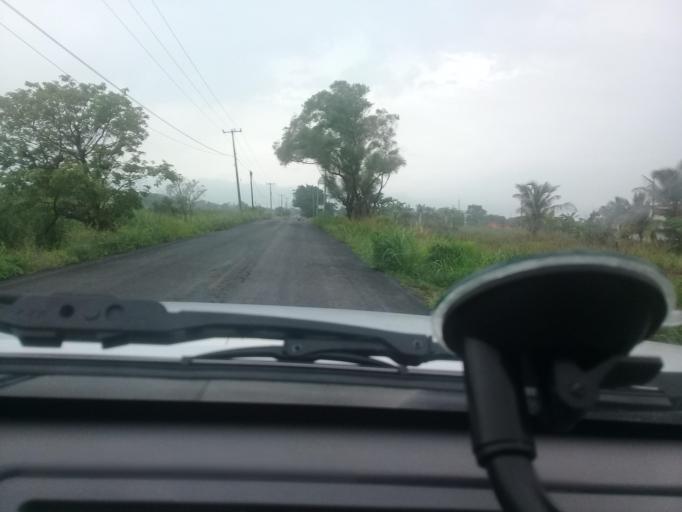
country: MX
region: Veracruz
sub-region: La Antigua
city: Nicolas Blanco (San Pancho)
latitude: 19.3565
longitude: -96.3527
